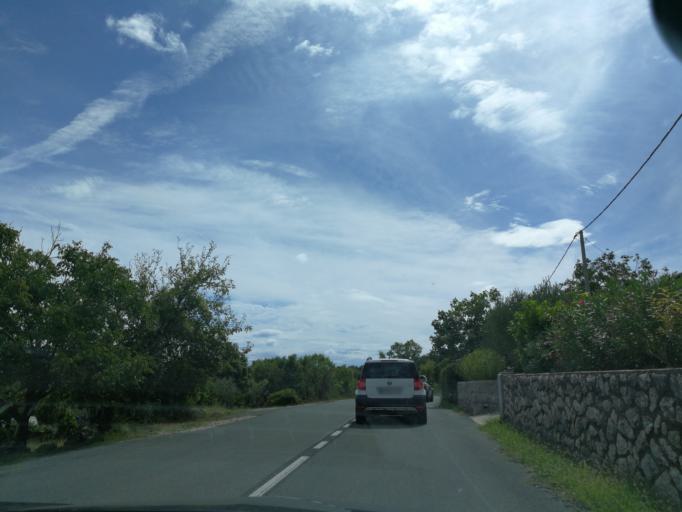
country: HR
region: Primorsko-Goranska
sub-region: Grad Crikvenica
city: Crikvenica
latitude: 45.1043
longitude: 14.6450
